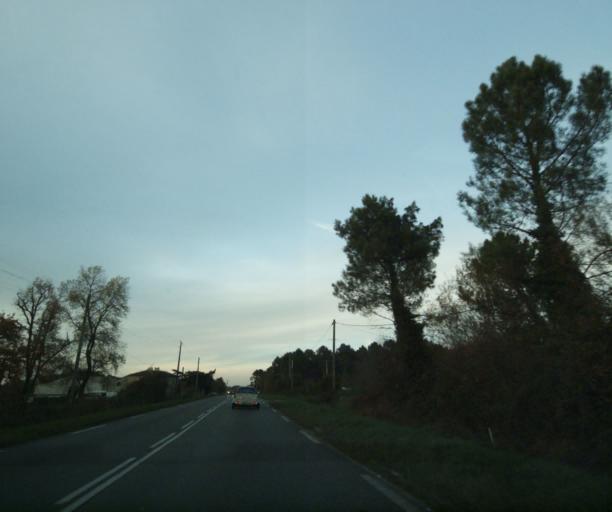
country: FR
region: Aquitaine
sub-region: Departement de la Gironde
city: Bazas
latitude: 44.4807
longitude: -0.2299
